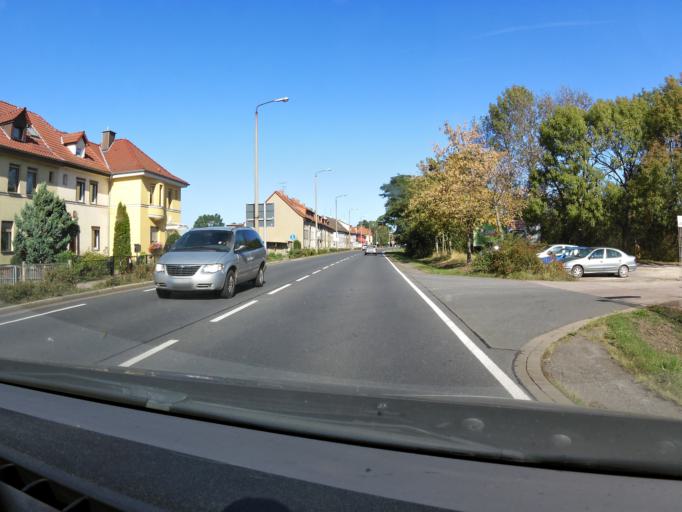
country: DE
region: Thuringia
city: Nordhausen
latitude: 51.4846
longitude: 10.8046
